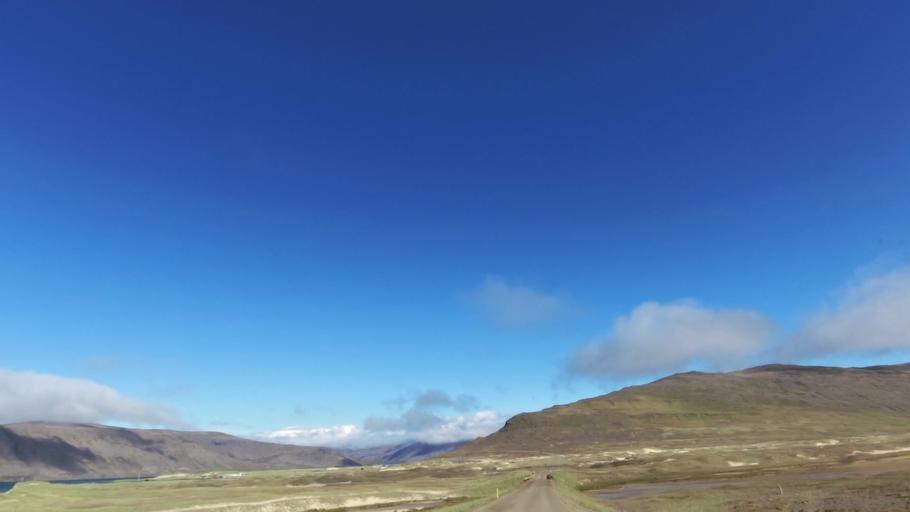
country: IS
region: West
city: Olafsvik
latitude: 65.5581
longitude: -23.9892
